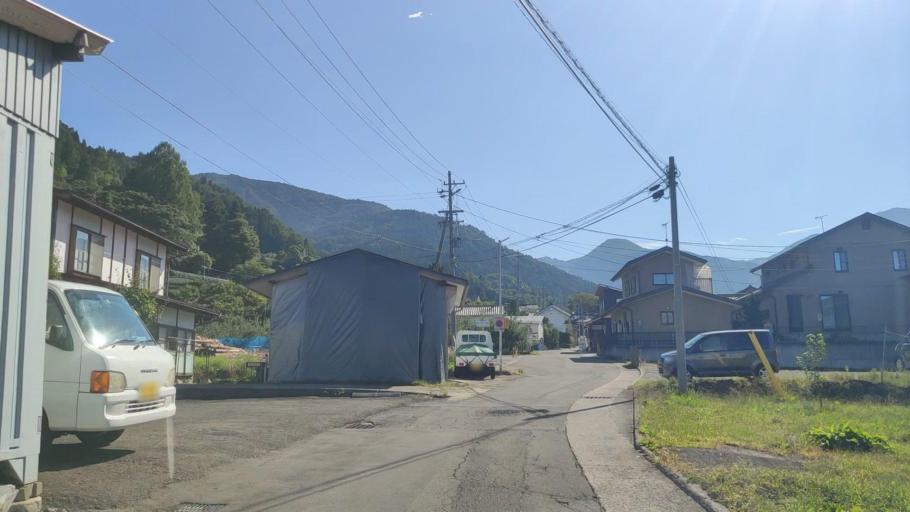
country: JP
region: Nagano
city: Nakano
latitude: 36.7364
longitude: 138.4254
